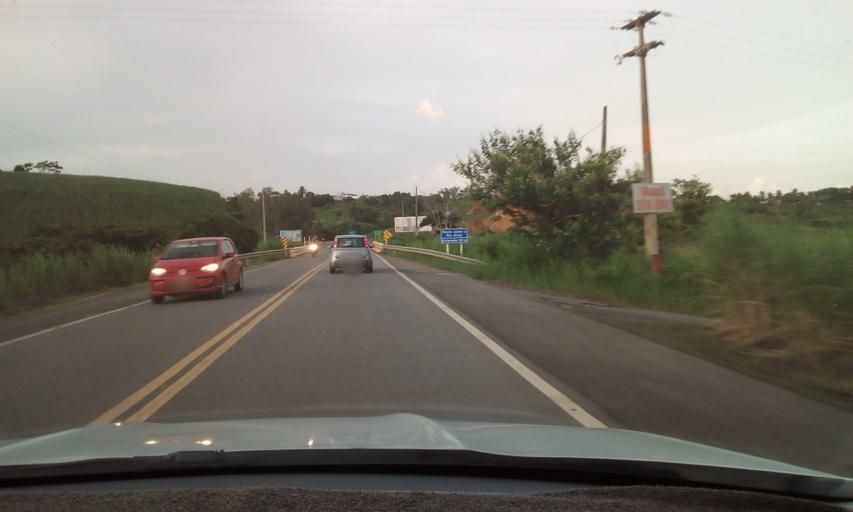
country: BR
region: Pernambuco
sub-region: Vicencia
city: Vicencia
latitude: -7.6181
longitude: -35.2406
